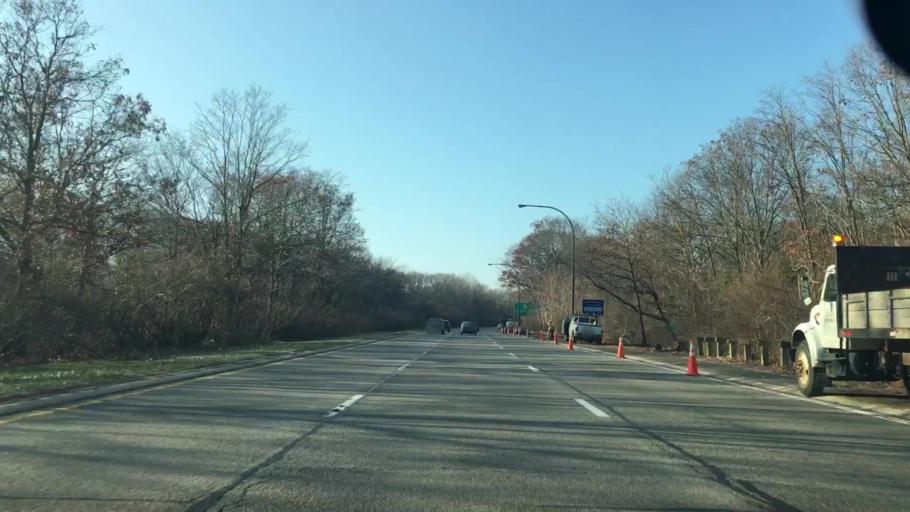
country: US
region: New York
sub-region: Suffolk County
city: Commack
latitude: 40.8210
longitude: -73.2662
